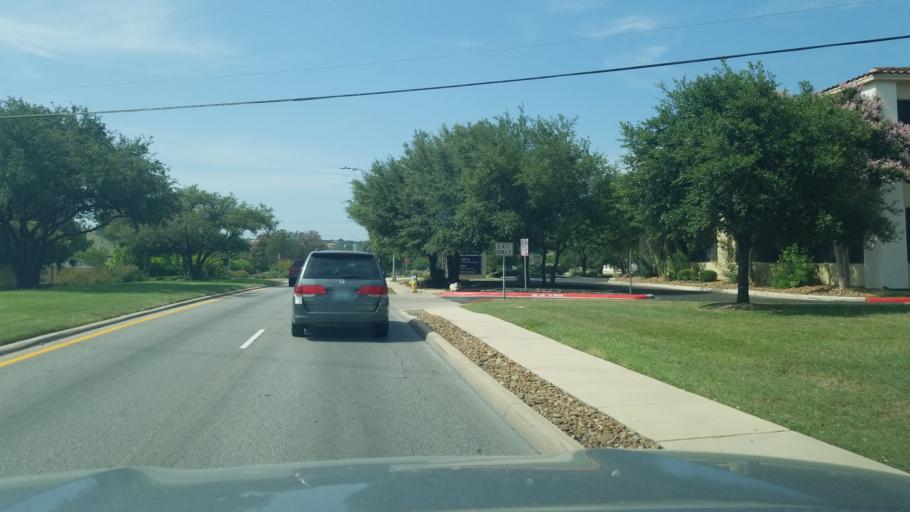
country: US
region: Texas
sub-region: Bexar County
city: Hollywood Park
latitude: 29.6182
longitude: -98.4941
